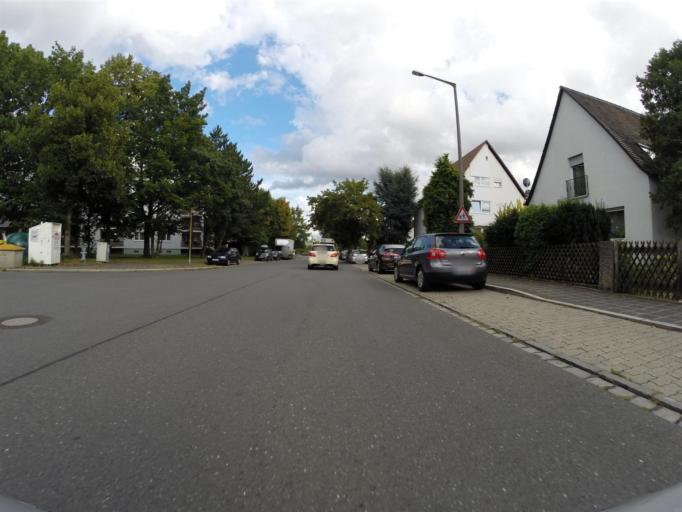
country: DE
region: Bavaria
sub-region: Regierungsbezirk Mittelfranken
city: Grossreuth bei Schweinau
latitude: 49.4228
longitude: 11.0289
